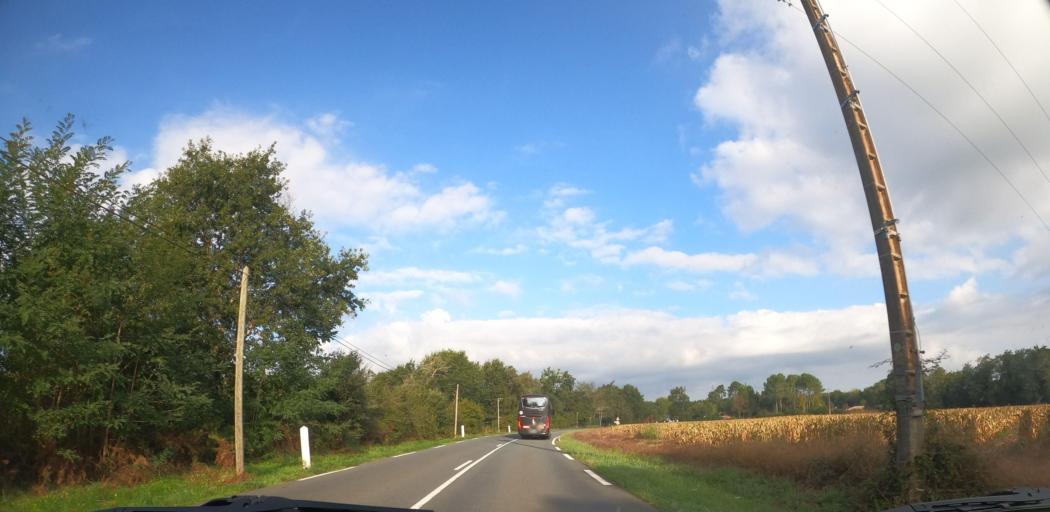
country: FR
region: Aquitaine
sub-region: Departement des Landes
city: Soustons
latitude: 43.7309
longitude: -1.2867
